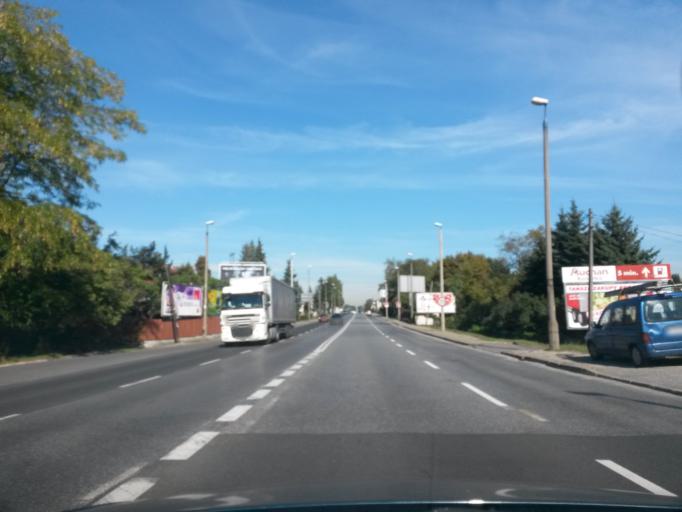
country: PL
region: Lesser Poland Voivodeship
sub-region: Powiat krakowski
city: Libertow
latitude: 49.9951
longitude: 19.9186
